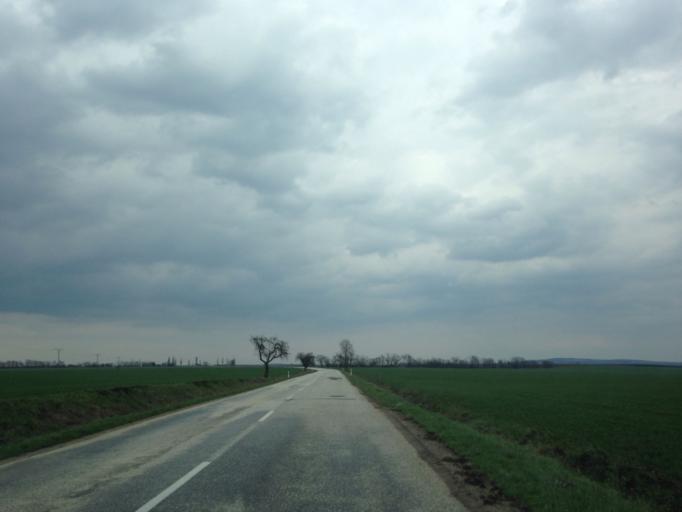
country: SK
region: Nitriansky
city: Svodin
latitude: 47.9833
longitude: 18.3660
